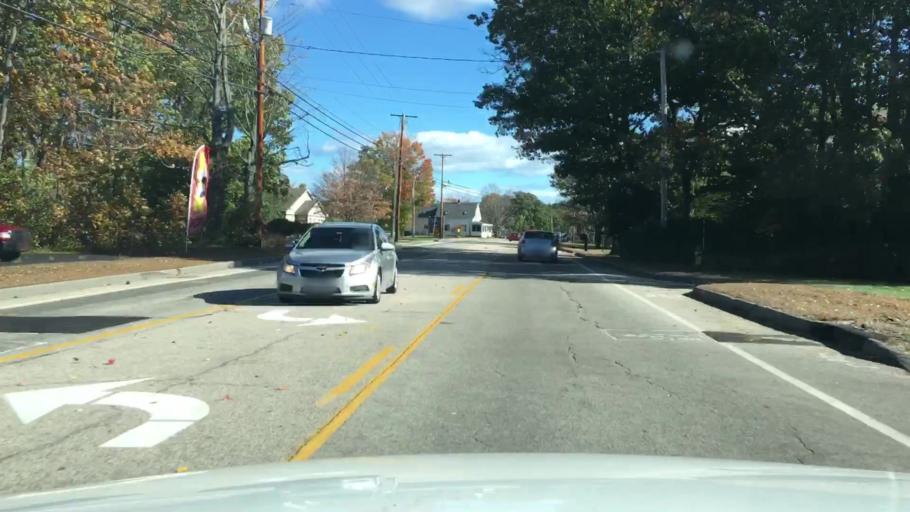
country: US
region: Maine
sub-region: York County
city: South Sanford
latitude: 43.4081
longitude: -70.7370
